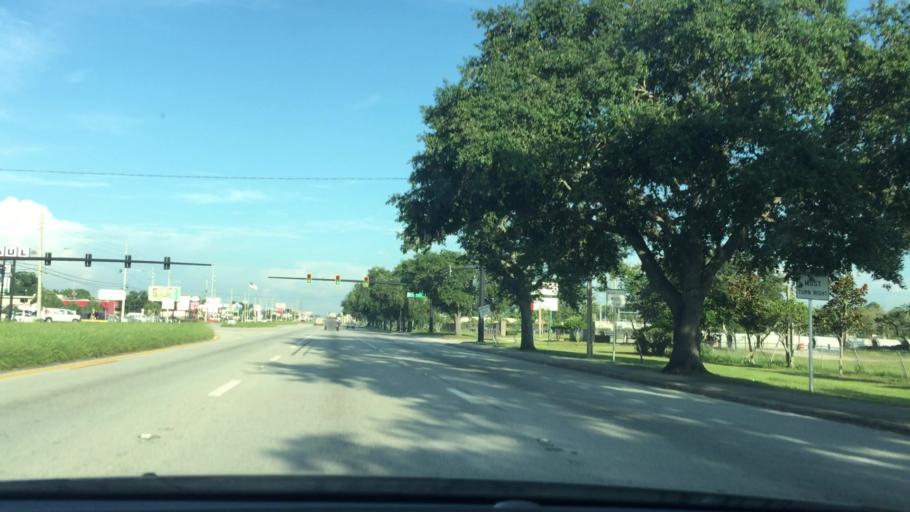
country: US
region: Florida
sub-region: Orange County
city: Pine Hills
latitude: 28.5527
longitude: -81.4378
